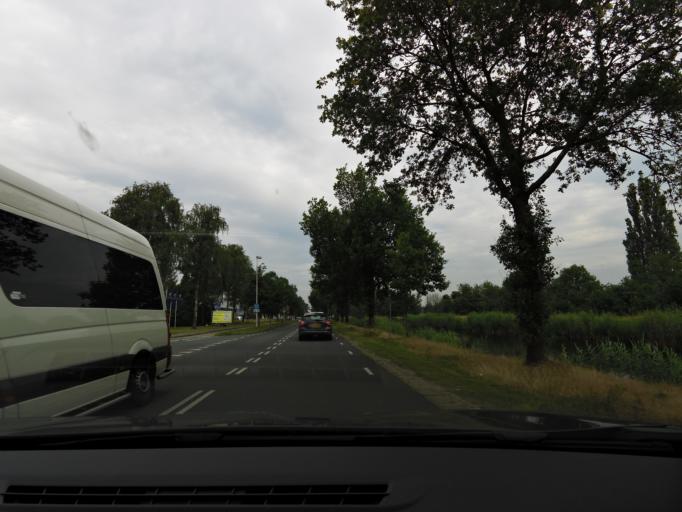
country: NL
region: Gelderland
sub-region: Gemeente Rheden
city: Spankeren
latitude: 52.0585
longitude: 6.1056
